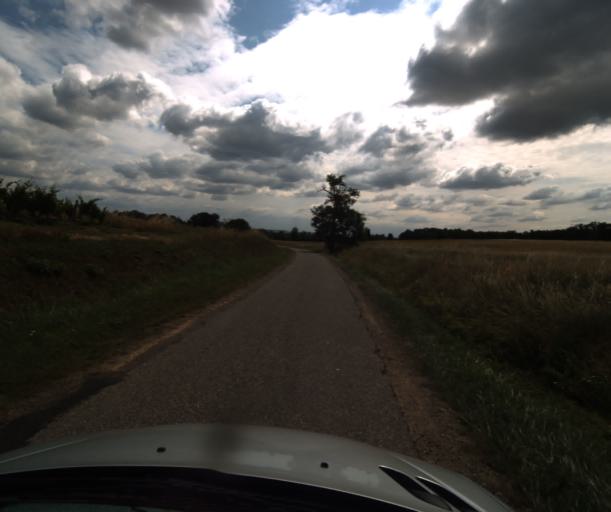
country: FR
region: Midi-Pyrenees
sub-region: Departement du Tarn-et-Garonne
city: Campsas
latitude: 43.9094
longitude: 1.3062
